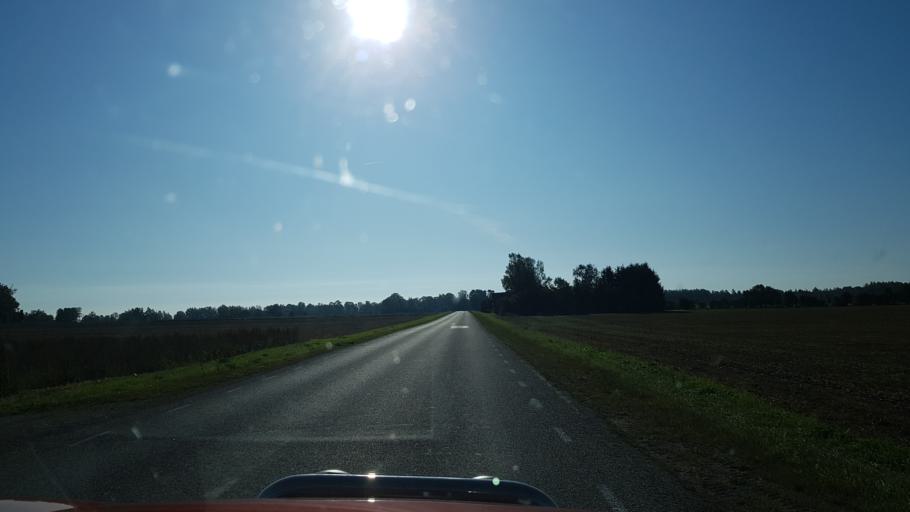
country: EE
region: Jogevamaa
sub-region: Tabivere vald
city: Tabivere
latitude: 58.6740
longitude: 26.6781
